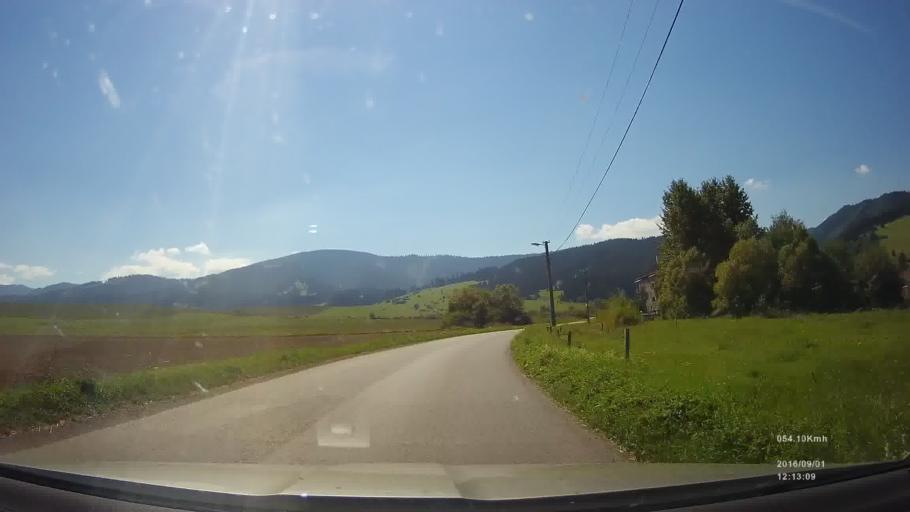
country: SK
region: Zilinsky
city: Ruzomberok
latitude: 49.0528
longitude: 19.4312
